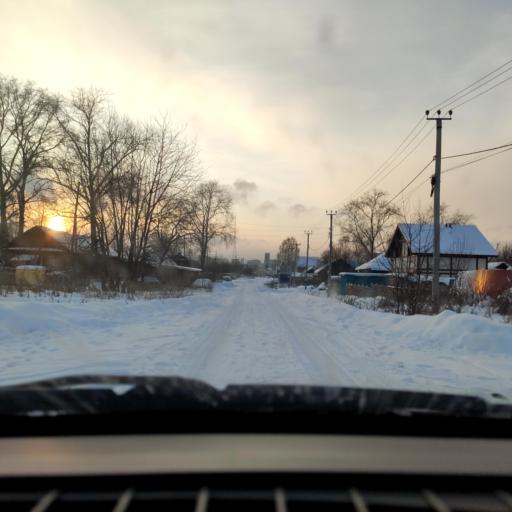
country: RU
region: Perm
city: Perm
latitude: 58.0198
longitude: 56.3296
